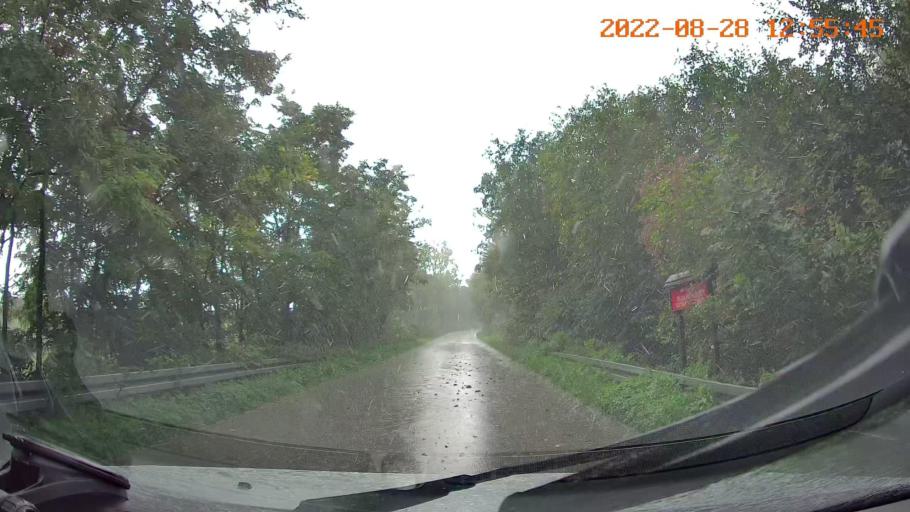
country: PL
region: Swietokrzyskie
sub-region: Powiat jedrzejowski
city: Wodzislaw
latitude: 50.3695
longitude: 20.2009
